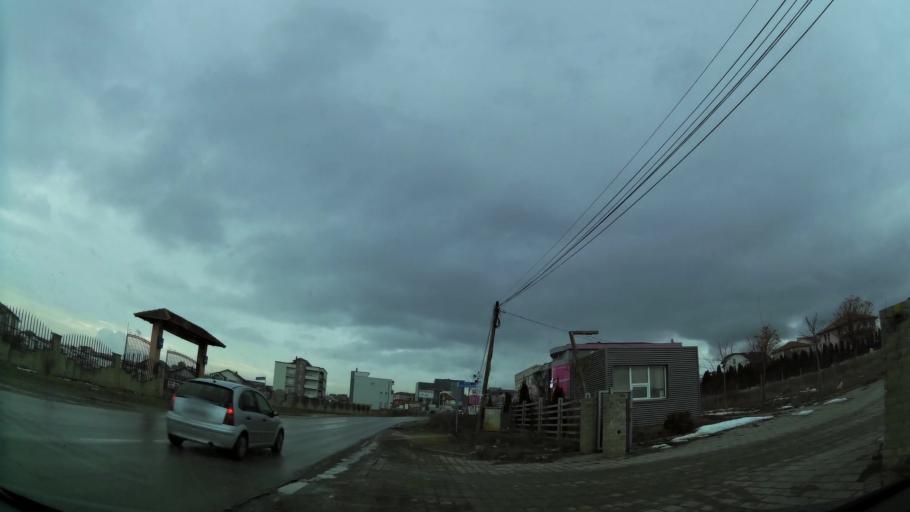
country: XK
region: Pristina
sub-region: Komuna e Prishtines
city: Pristina
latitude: 42.6240
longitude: 21.1612
